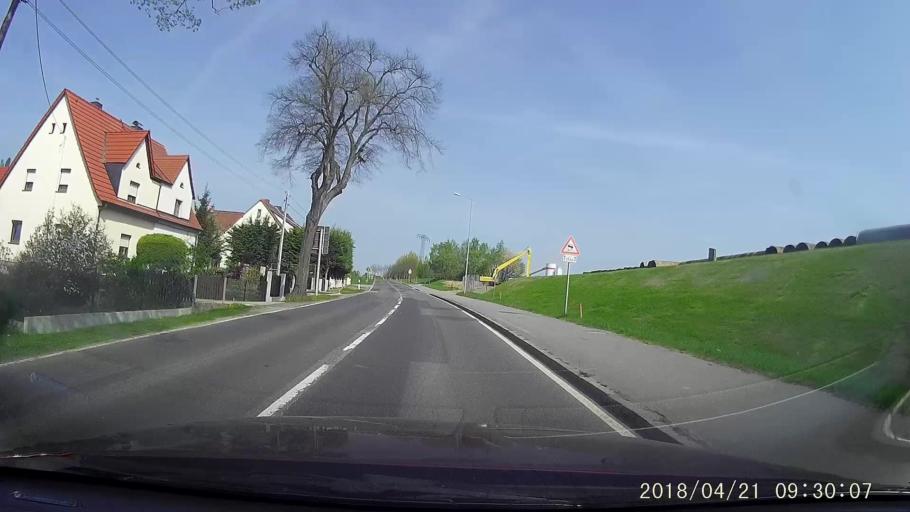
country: DE
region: Saxony
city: Bautzen
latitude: 51.1972
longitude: 14.4087
